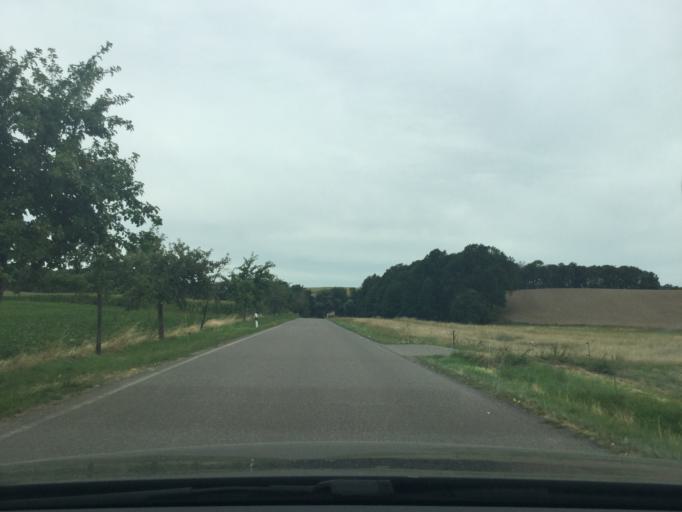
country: DE
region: Saxony
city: Wilsdruff
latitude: 51.0654
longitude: 13.5918
